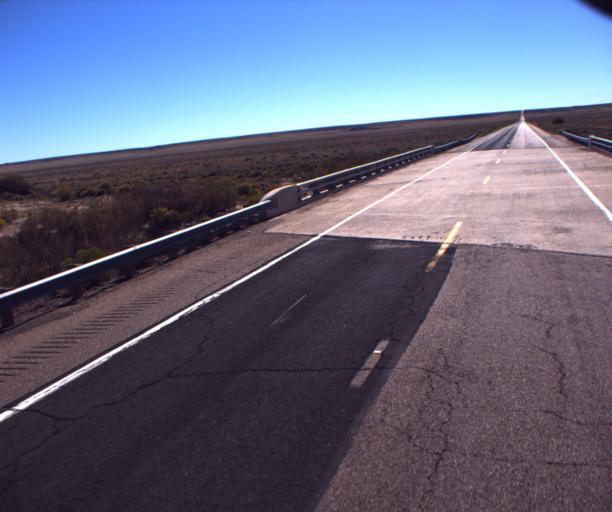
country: US
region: Arizona
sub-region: Navajo County
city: Snowflake
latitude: 34.7446
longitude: -109.7959
